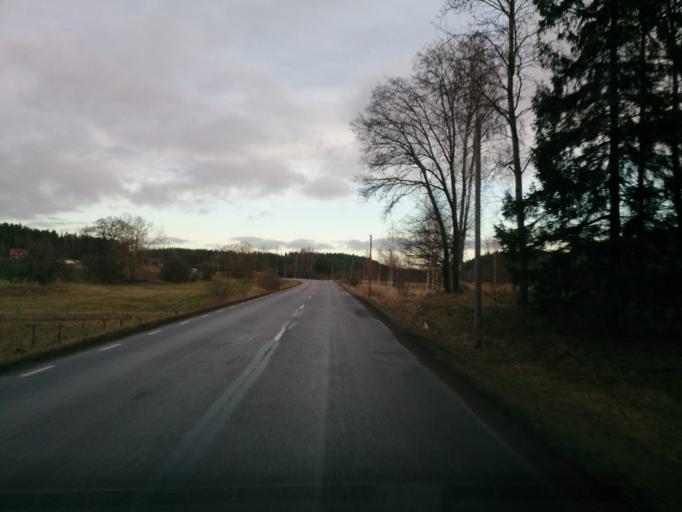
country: SE
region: OEstergoetland
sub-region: Atvidabergs Kommun
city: Atvidaberg
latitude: 58.3444
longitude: 16.0284
